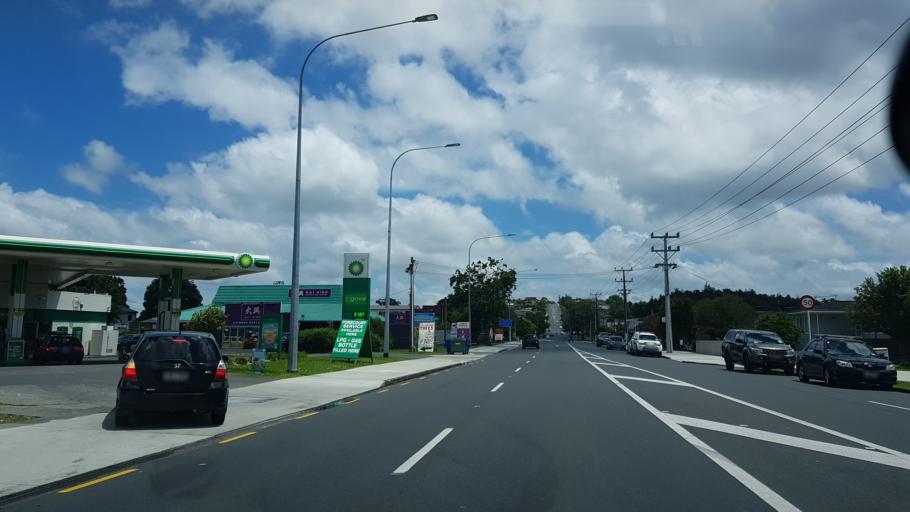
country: NZ
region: Auckland
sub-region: Auckland
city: North Shore
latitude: -36.7928
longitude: 174.7467
